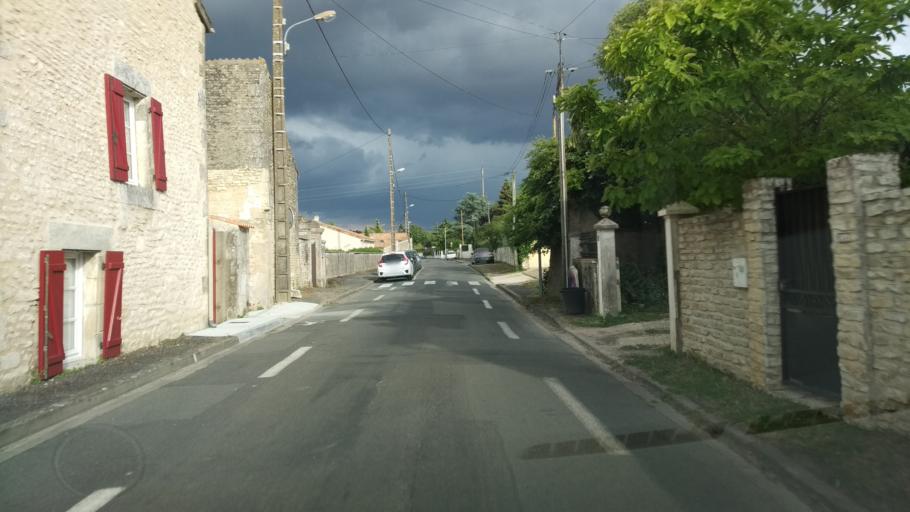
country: FR
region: Poitou-Charentes
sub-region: Departement de la Vienne
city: Migne-Auxances
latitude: 46.6280
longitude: 0.3369
